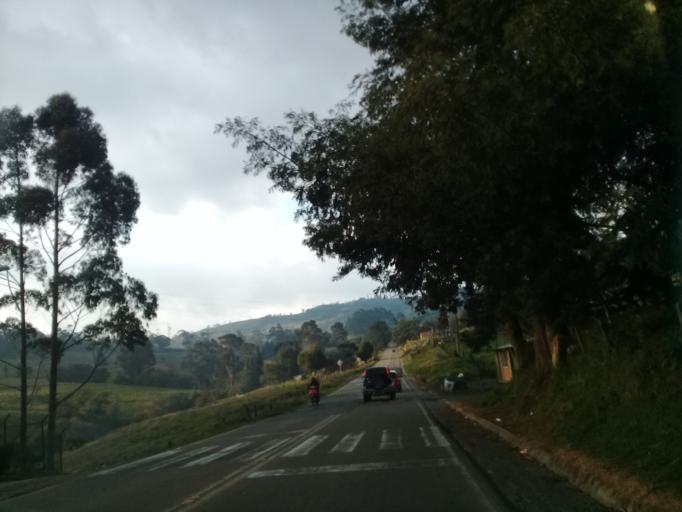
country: CO
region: Cundinamarca
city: Zipaquira
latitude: 5.0706
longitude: -74.0542
